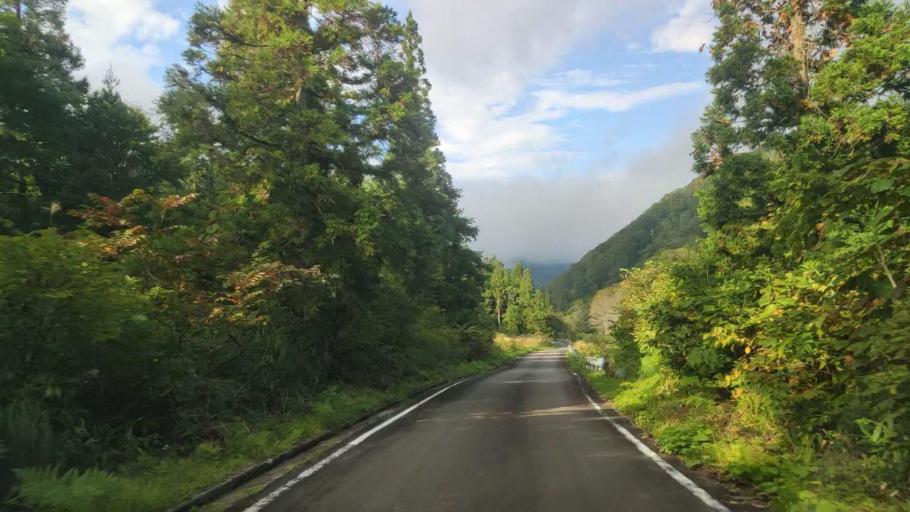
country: JP
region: Toyama
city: Yatsuomachi-higashikumisaka
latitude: 36.3702
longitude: 137.0772
